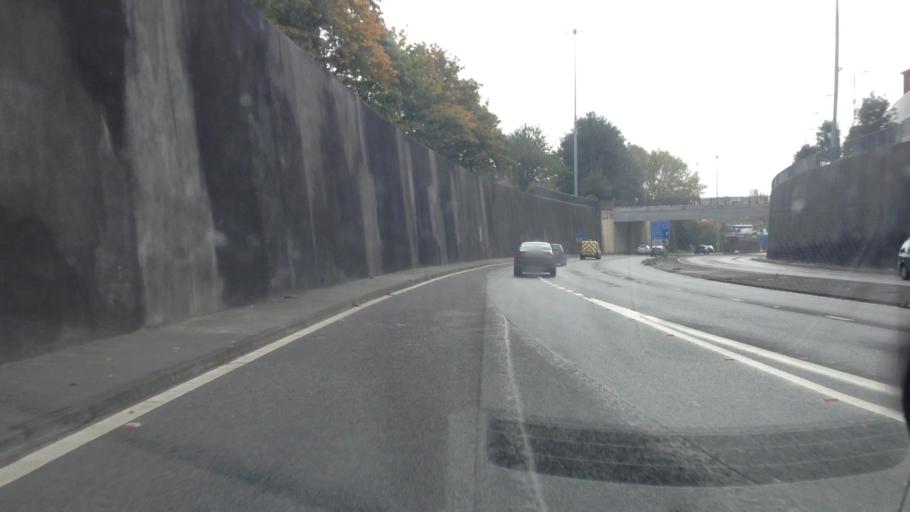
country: GB
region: England
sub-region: City and Borough of Leeds
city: Leeds
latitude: 53.8043
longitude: -1.5414
